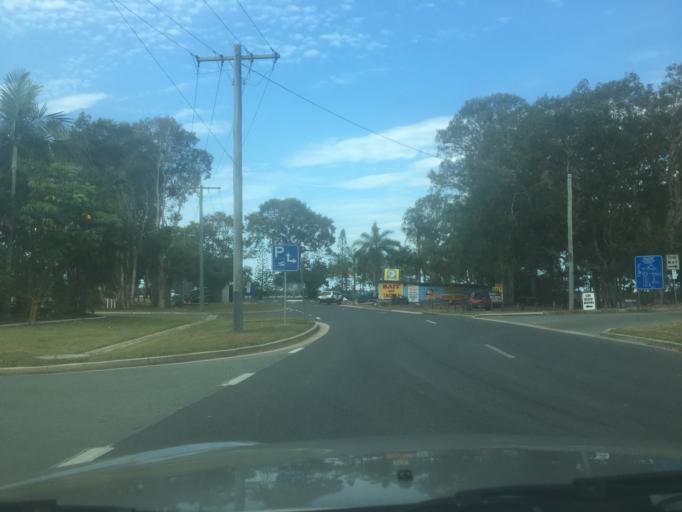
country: AU
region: Queensland
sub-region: Moreton Bay
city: Bongaree
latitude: -27.0687
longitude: 153.1333
